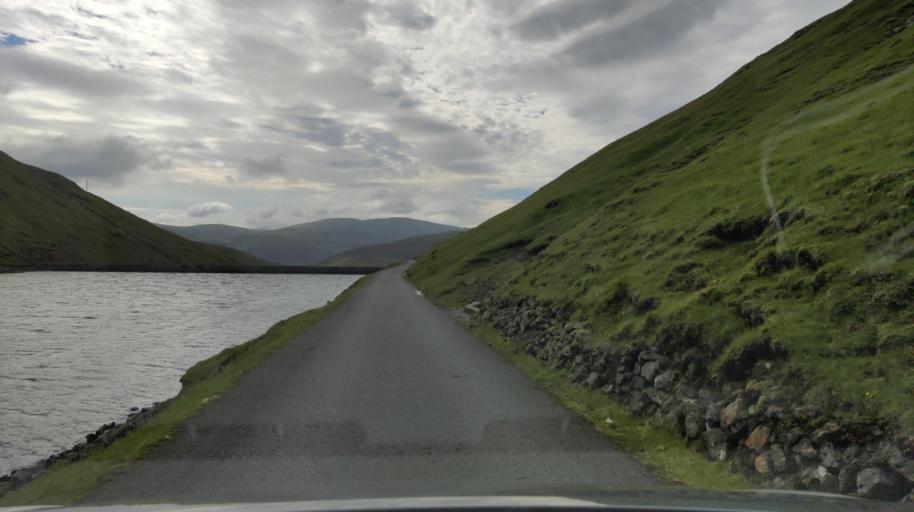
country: FO
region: Streymoy
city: Vestmanna
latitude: 62.1545
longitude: -7.1245
